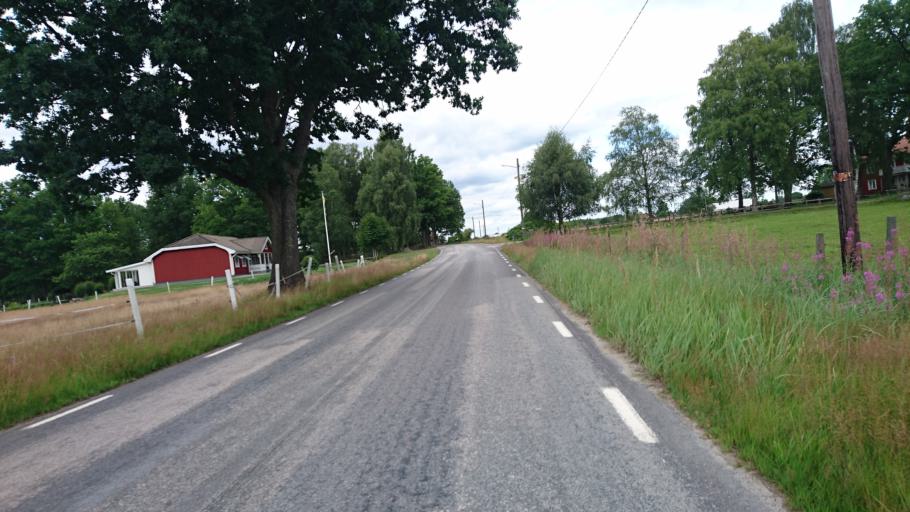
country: SE
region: Kronoberg
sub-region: Alvesta Kommun
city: Moheda
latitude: 56.9833
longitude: 14.5818
